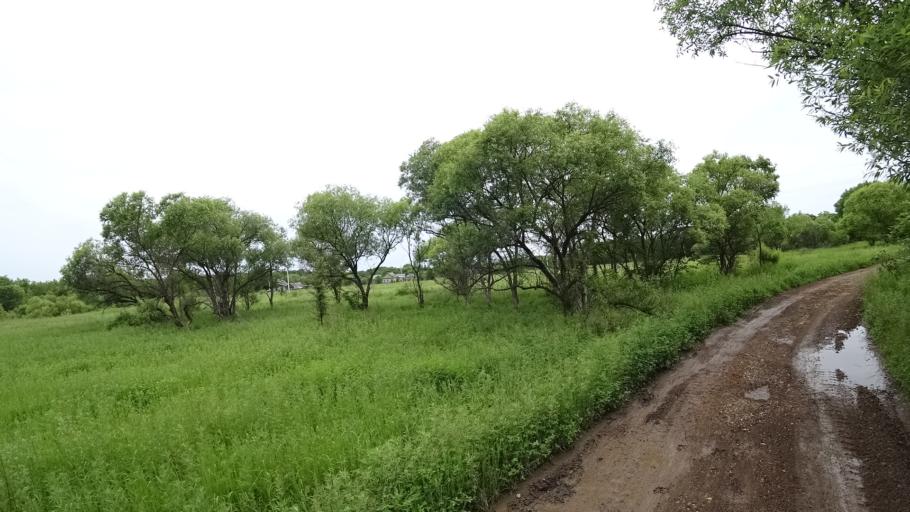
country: RU
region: Primorskiy
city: Novosysoyevka
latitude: 44.2083
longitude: 133.3284
